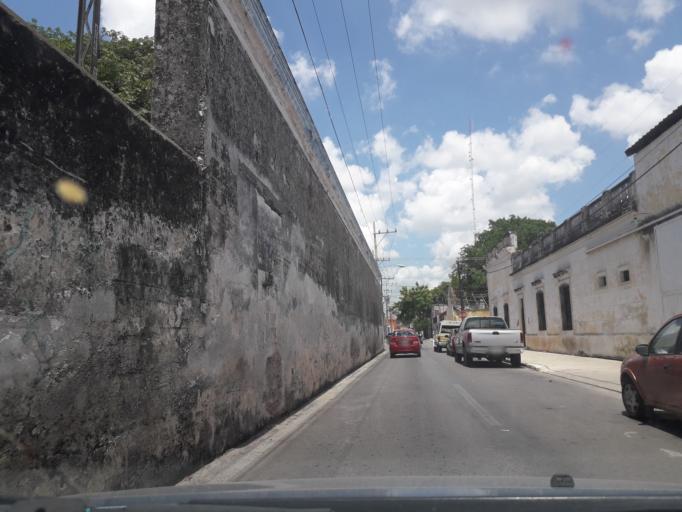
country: MX
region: Yucatan
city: Merida
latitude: 20.9593
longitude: -89.6203
